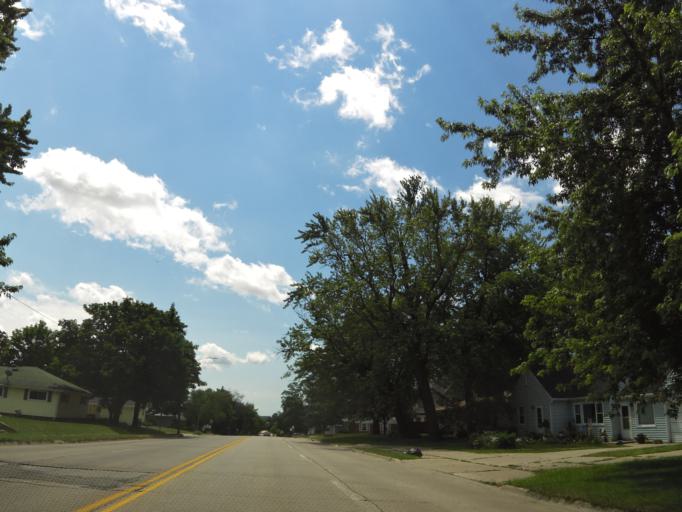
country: US
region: Iowa
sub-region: Fayette County
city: Oelwein
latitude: 42.6891
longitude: -91.9133
